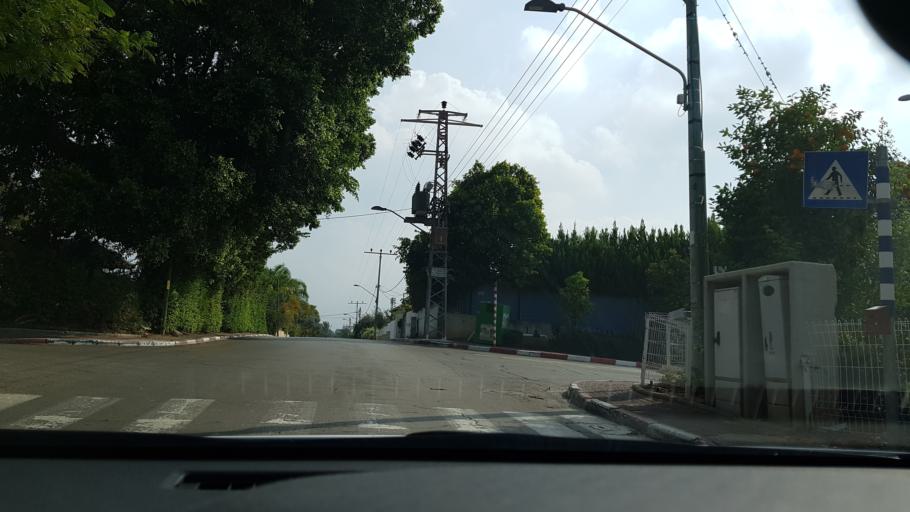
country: IL
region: Central District
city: Mazkeret Batya
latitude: 31.8740
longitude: 34.8171
